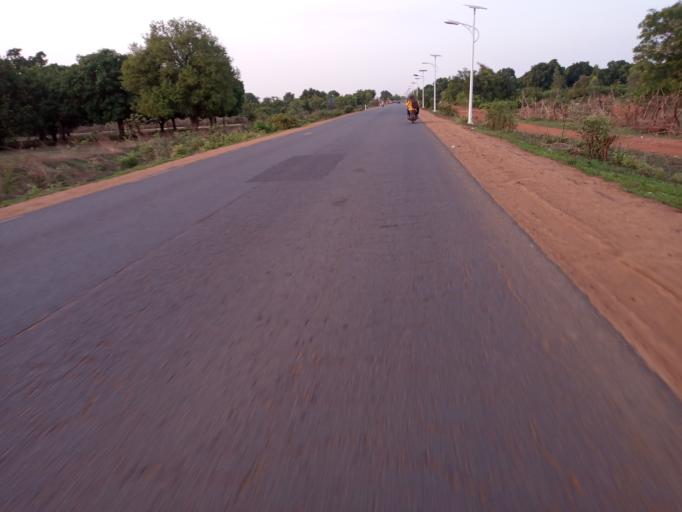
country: ML
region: Bamako
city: Bamako
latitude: 12.3023
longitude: -8.1576
